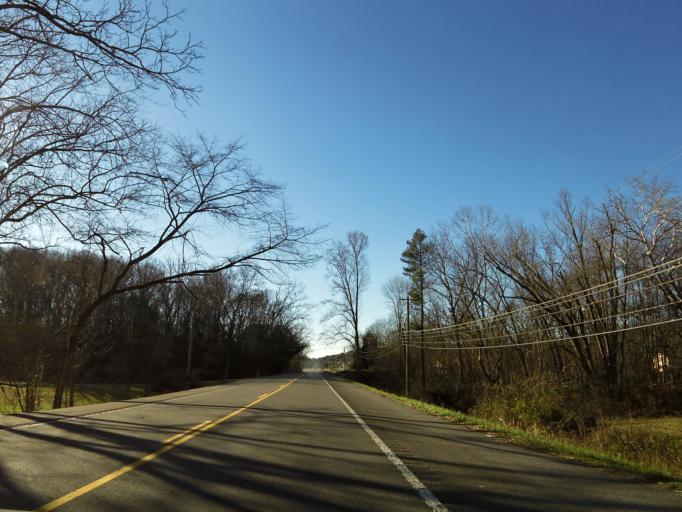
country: US
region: Tennessee
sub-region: Knox County
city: Farragut
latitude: 35.9785
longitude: -84.1291
